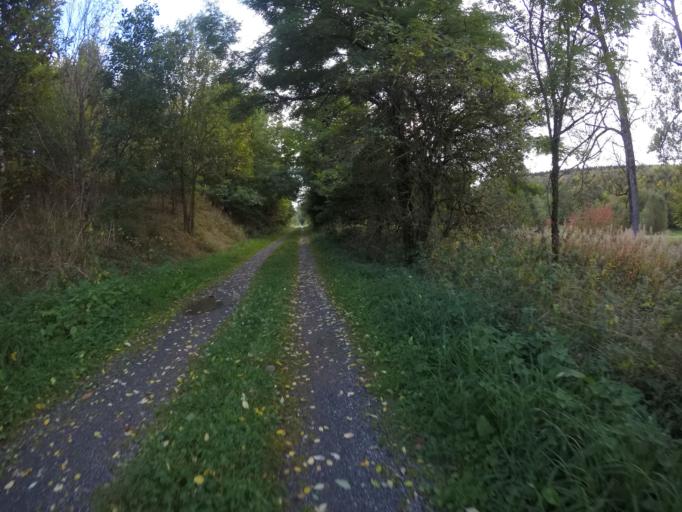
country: BE
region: Wallonia
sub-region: Province du Luxembourg
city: Fauvillers
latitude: 49.9197
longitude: 5.6926
